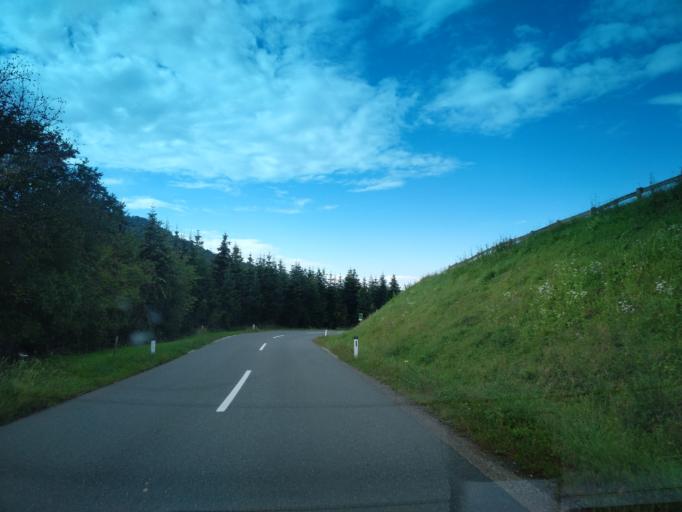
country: AT
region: Styria
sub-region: Politischer Bezirk Leibnitz
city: Leibnitz
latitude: 46.7829
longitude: 15.5229
